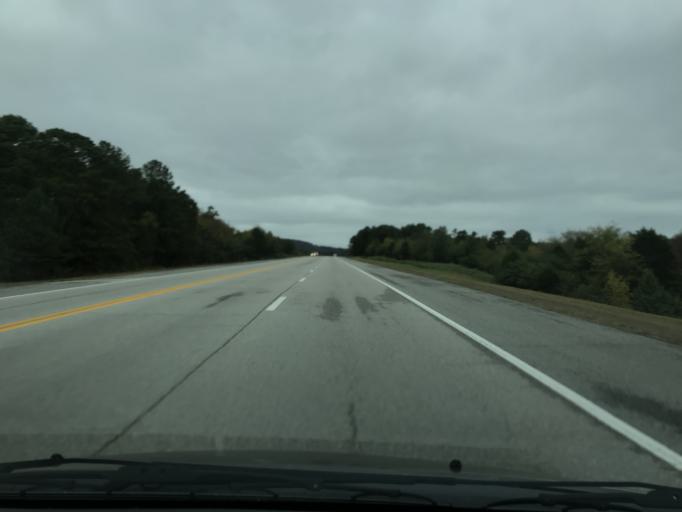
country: US
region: Tennessee
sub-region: Rhea County
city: Dayton
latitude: 35.4619
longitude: -85.0153
